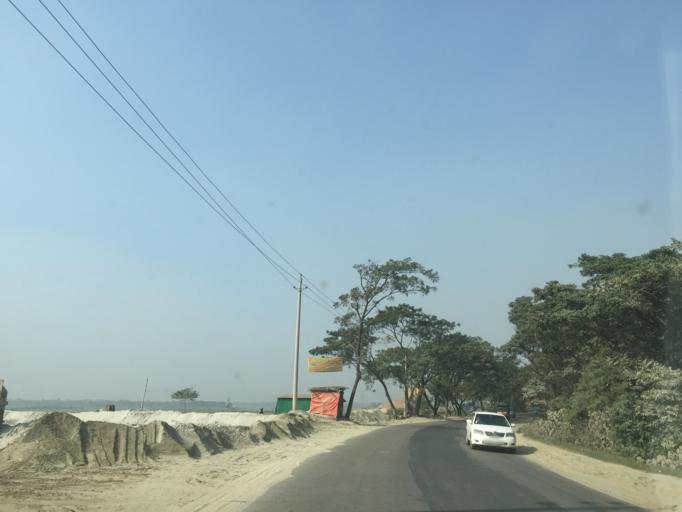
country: BD
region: Dhaka
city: Tungi
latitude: 23.8313
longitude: 90.3408
